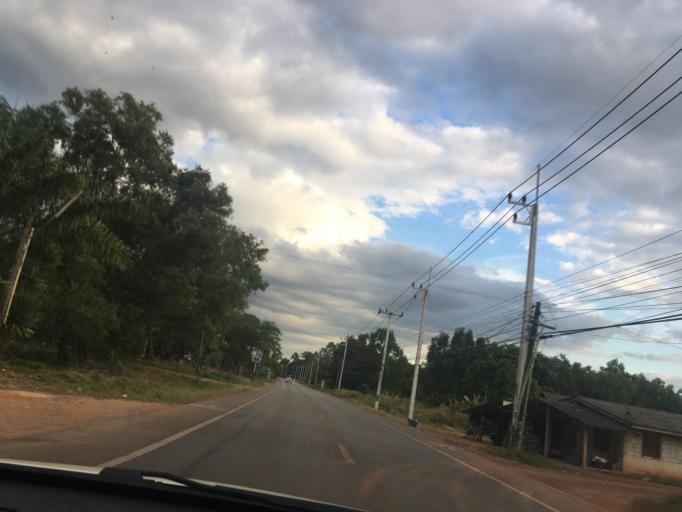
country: TH
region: Chanthaburi
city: Na Yai Am
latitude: 12.6940
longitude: 101.8060
